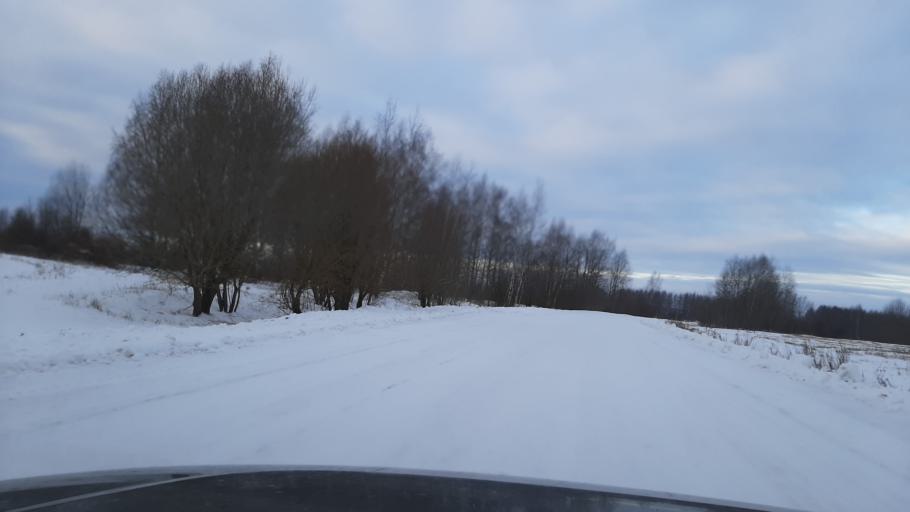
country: RU
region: Kostroma
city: Kosmynino
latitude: 57.4791
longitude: 40.8532
